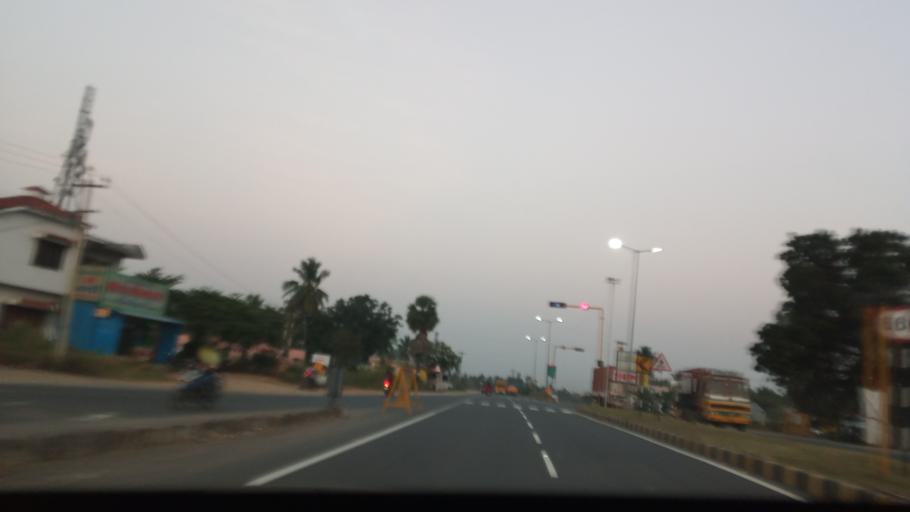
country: IN
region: Tamil Nadu
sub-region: Salem
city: Belur
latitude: 11.6578
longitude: 78.4209
